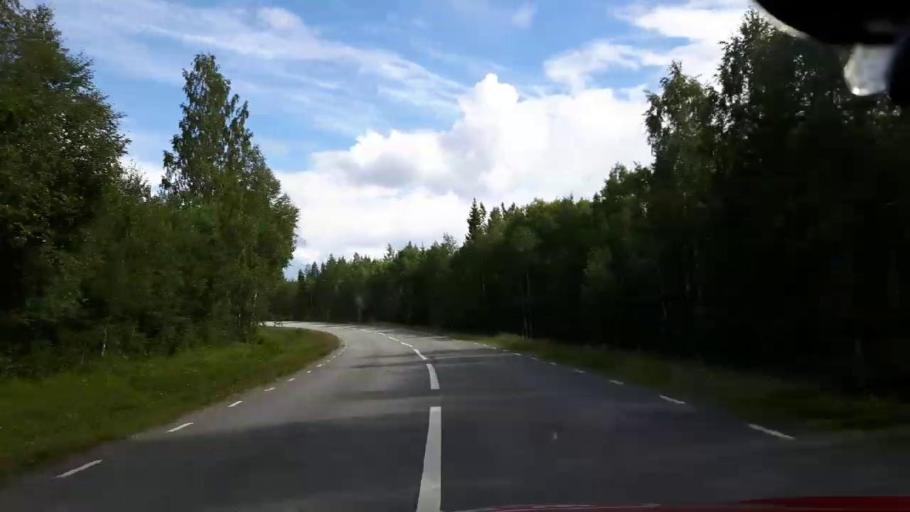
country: SE
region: Jaemtland
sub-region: Stroemsunds Kommun
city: Stroemsund
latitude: 64.3420
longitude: 15.1119
